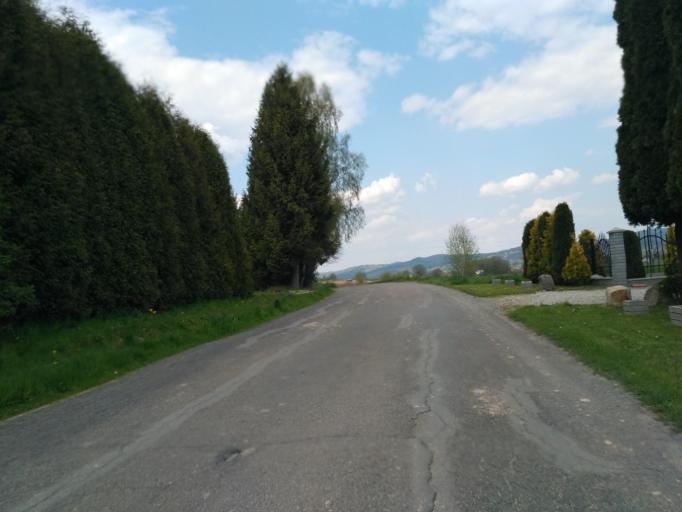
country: PL
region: Subcarpathian Voivodeship
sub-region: Powiat krosnienski
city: Wojaszowka
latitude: 49.7661
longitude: 21.6718
